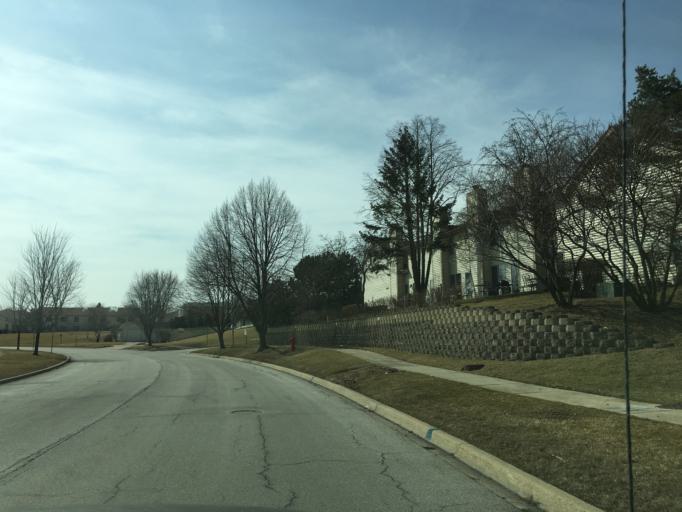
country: US
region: Illinois
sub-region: Cook County
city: Hoffman Estates
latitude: 42.0449
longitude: -88.0868
